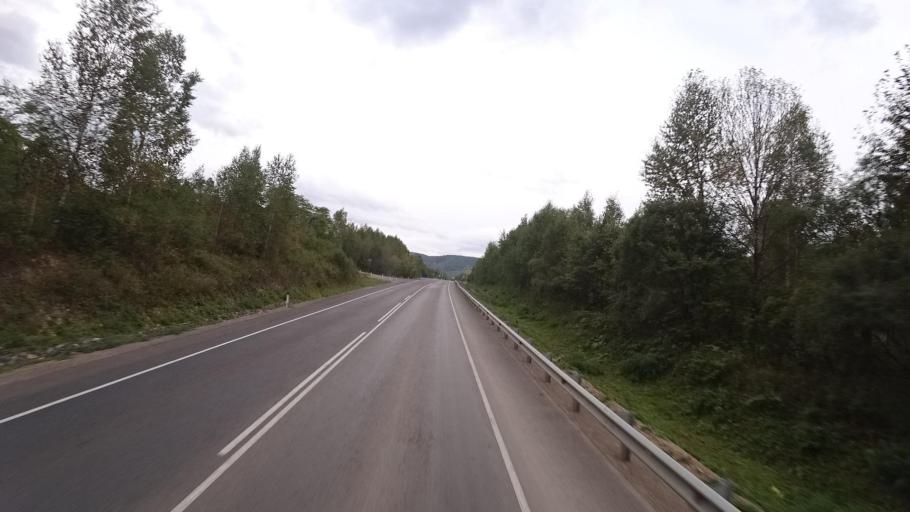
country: RU
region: Jewish Autonomous Oblast
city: Khingansk
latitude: 48.9882
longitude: 131.1315
